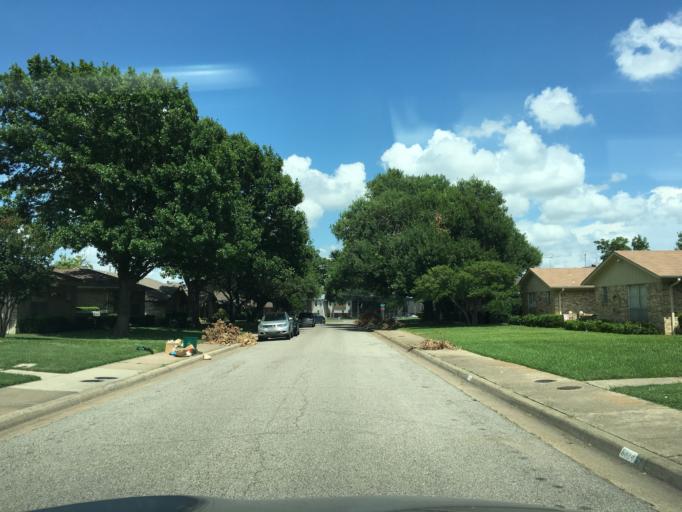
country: US
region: Texas
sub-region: Dallas County
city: Highland Park
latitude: 32.8545
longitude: -96.7542
